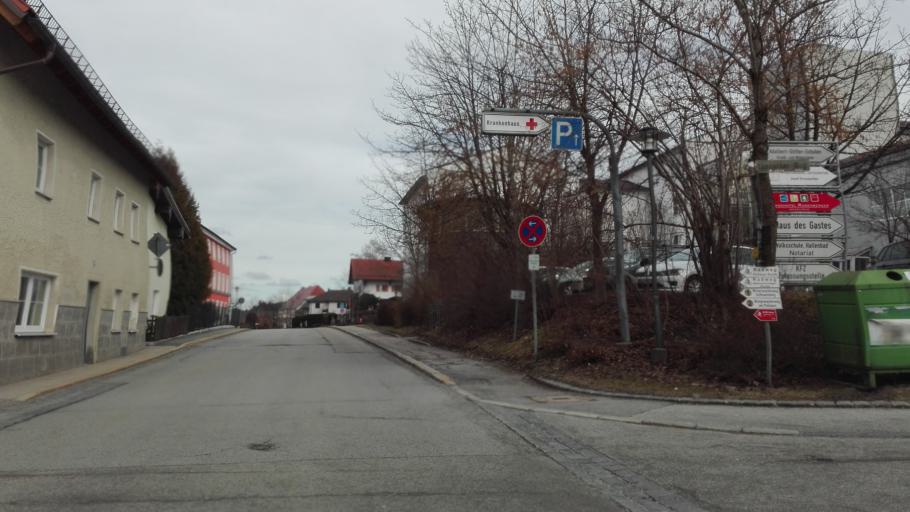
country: DE
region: Bavaria
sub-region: Lower Bavaria
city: Wegscheid
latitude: 48.6016
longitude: 13.7920
